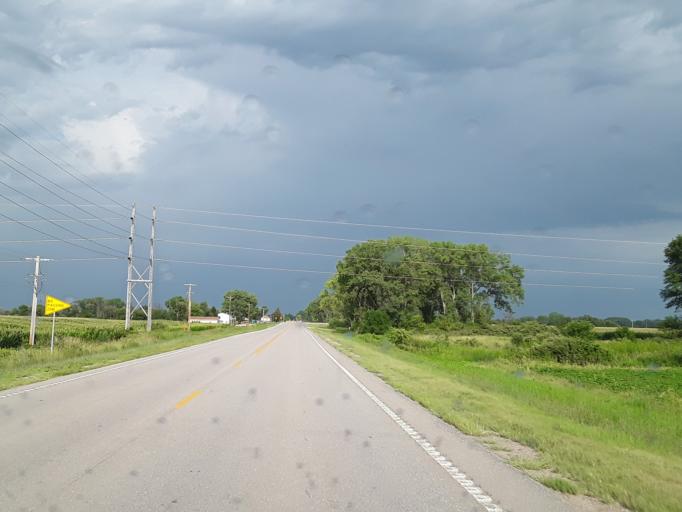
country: US
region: Nebraska
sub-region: Saunders County
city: Ashland
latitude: 41.0886
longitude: -96.3788
